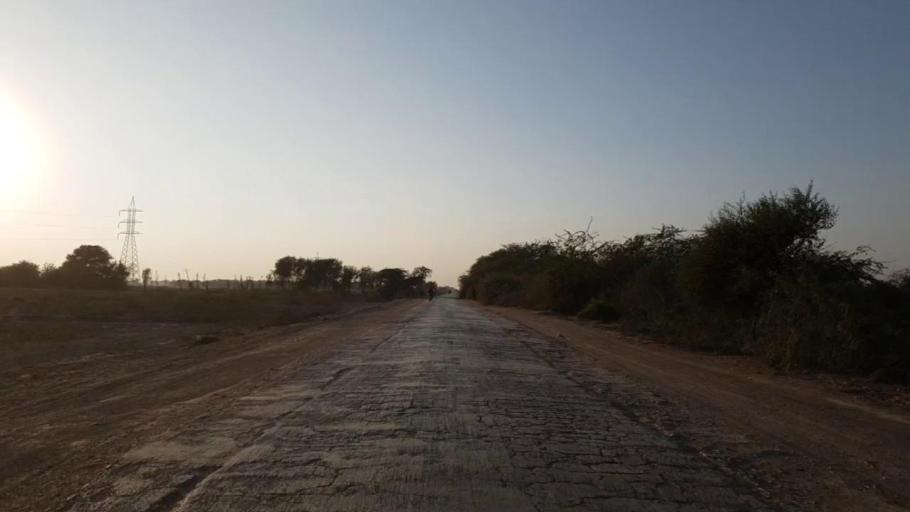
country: PK
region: Sindh
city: Chambar
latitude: 25.2204
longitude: 68.7400
